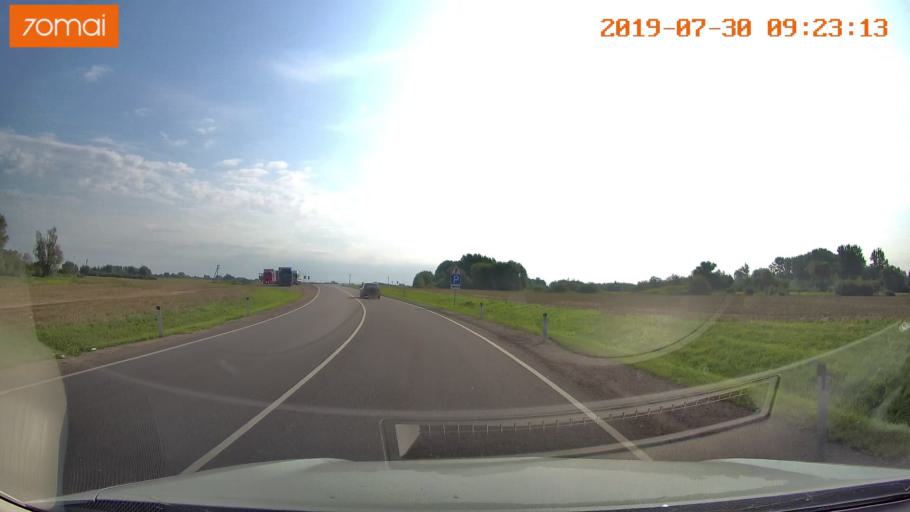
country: LT
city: Kybartai
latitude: 54.6327
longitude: 22.6712
